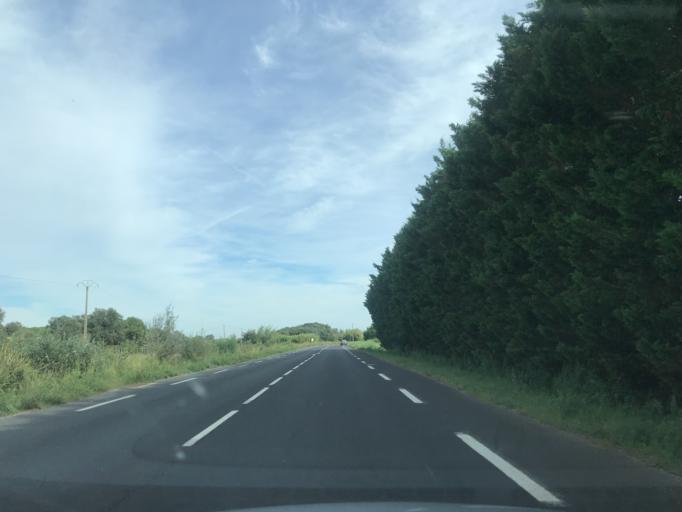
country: FR
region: Languedoc-Roussillon
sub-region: Departement du Gard
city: Aigues-Mortes
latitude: 43.5827
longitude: 4.2495
